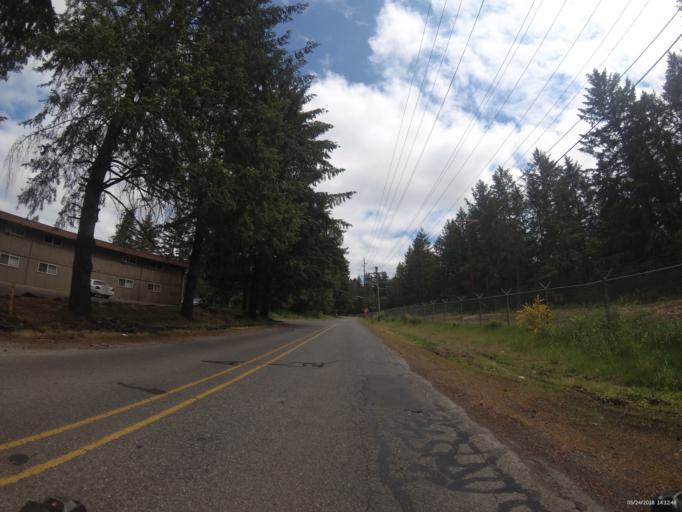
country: US
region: Washington
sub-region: Pierce County
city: McChord Air Force Base
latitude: 47.1400
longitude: -122.5120
